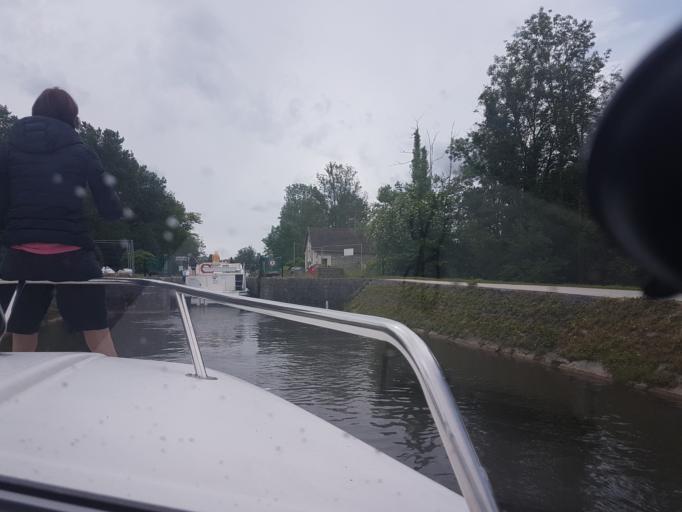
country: FR
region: Bourgogne
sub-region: Departement de l'Yonne
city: Augy
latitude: 47.7856
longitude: 3.5931
